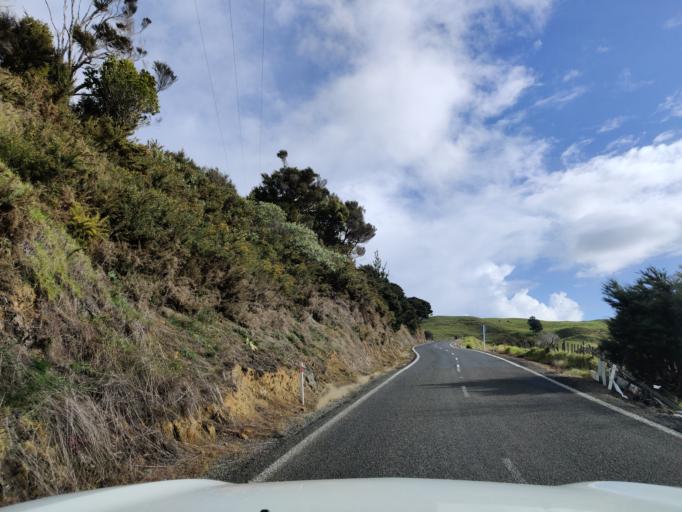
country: NZ
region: Waikato
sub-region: Thames-Coromandel District
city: Coromandel
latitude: -36.8157
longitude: 175.4865
